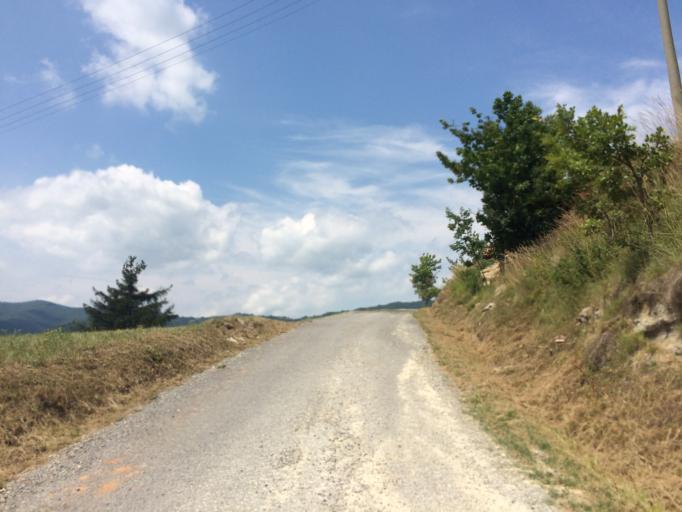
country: IT
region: Liguria
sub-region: Provincia di Savona
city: Massimino
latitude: 44.3148
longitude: 8.0612
